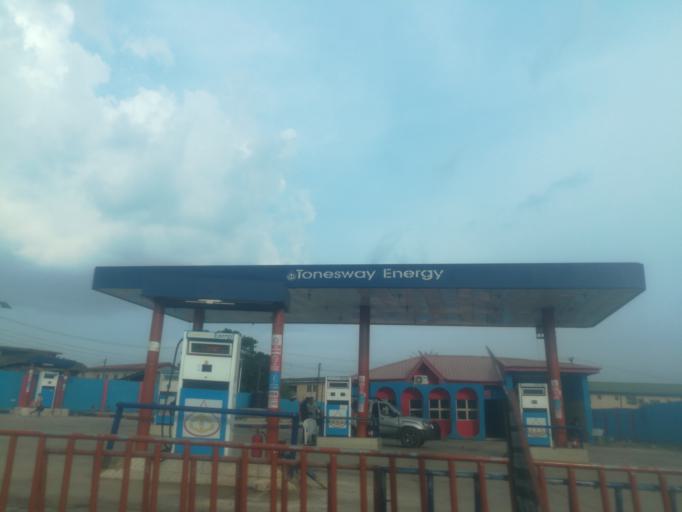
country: NG
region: Ogun
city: Abeokuta
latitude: 7.1589
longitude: 3.3109
